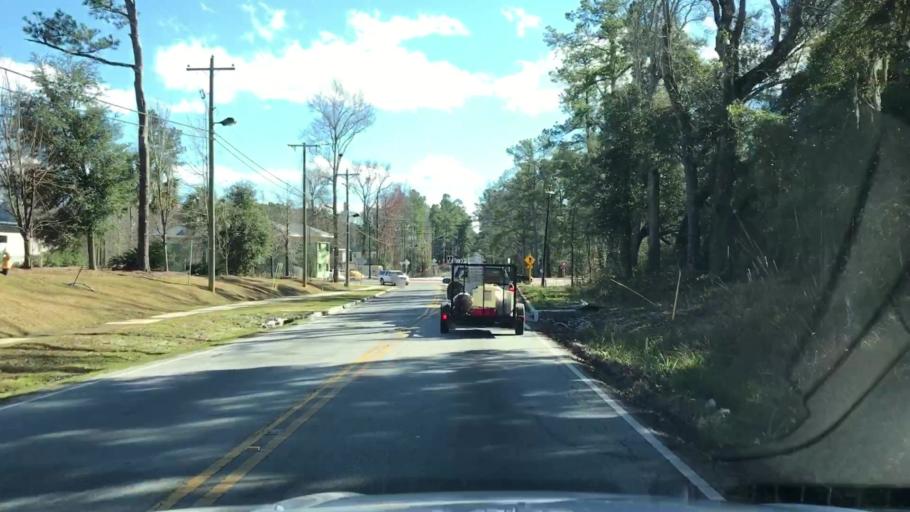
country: US
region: South Carolina
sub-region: Dorchester County
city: Summerville
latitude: 33.0235
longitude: -80.2422
